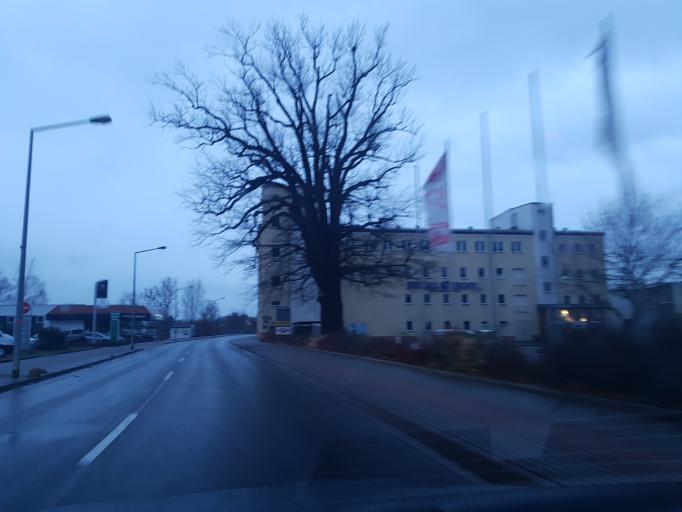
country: DE
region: Saxony
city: Grossenhain
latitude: 51.2878
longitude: 13.5234
